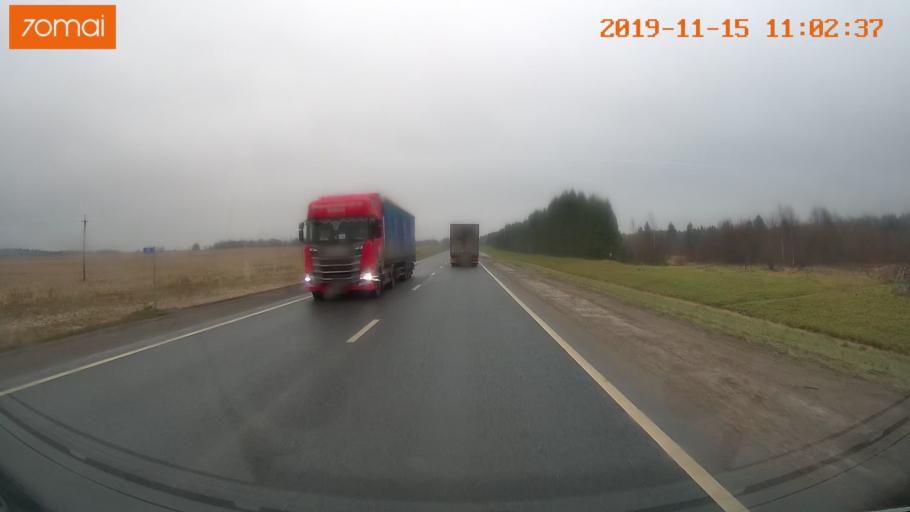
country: RU
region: Vologda
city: Chebsara
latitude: 59.1285
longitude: 38.9422
